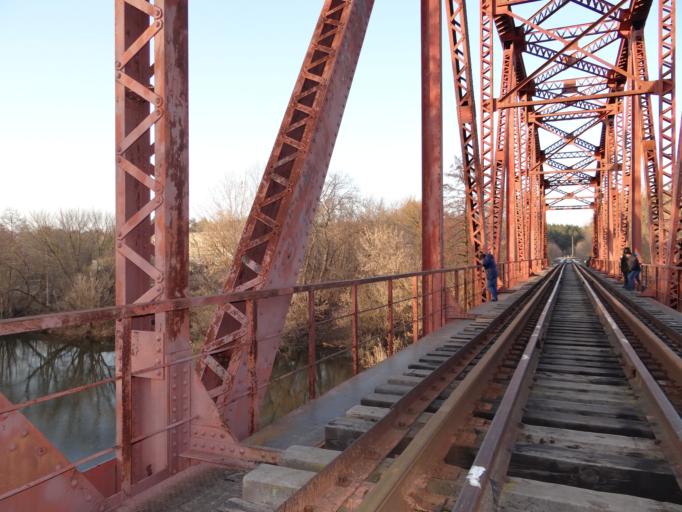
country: RU
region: Kursk
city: Kursk
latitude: 51.6862
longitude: 36.1128
